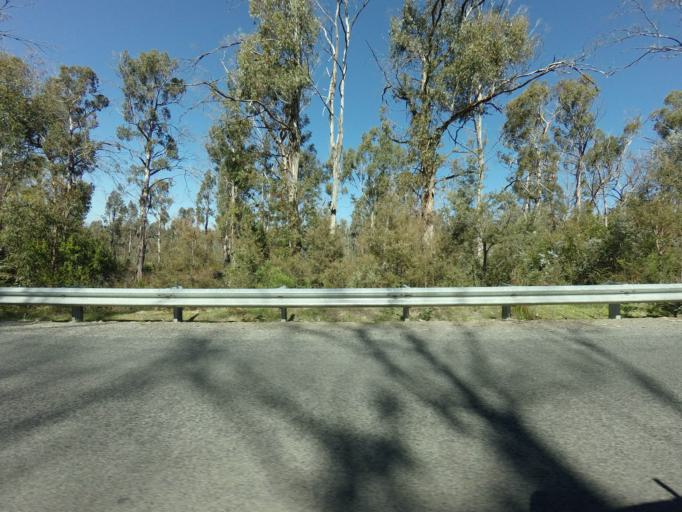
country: AU
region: Tasmania
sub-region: Derwent Valley
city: New Norfolk
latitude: -42.5449
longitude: 146.7167
